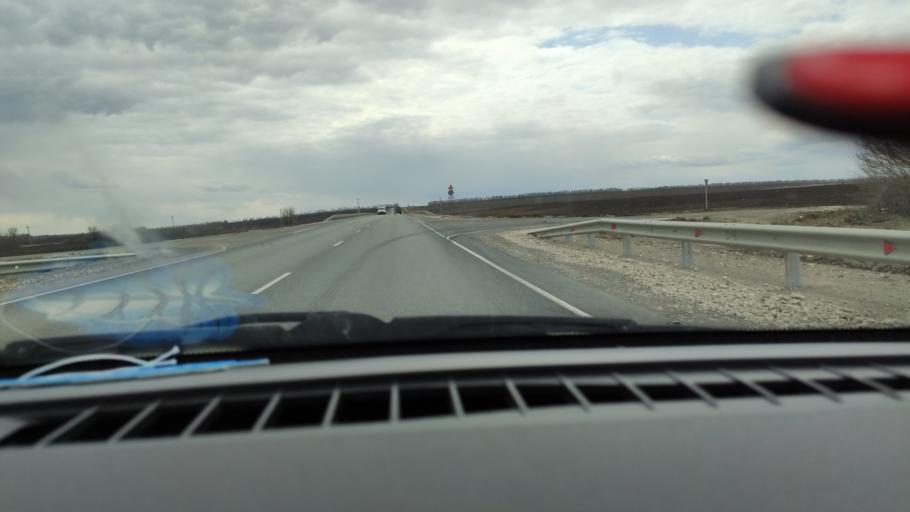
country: RU
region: Saratov
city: Yelshanka
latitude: 51.8421
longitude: 46.4791
